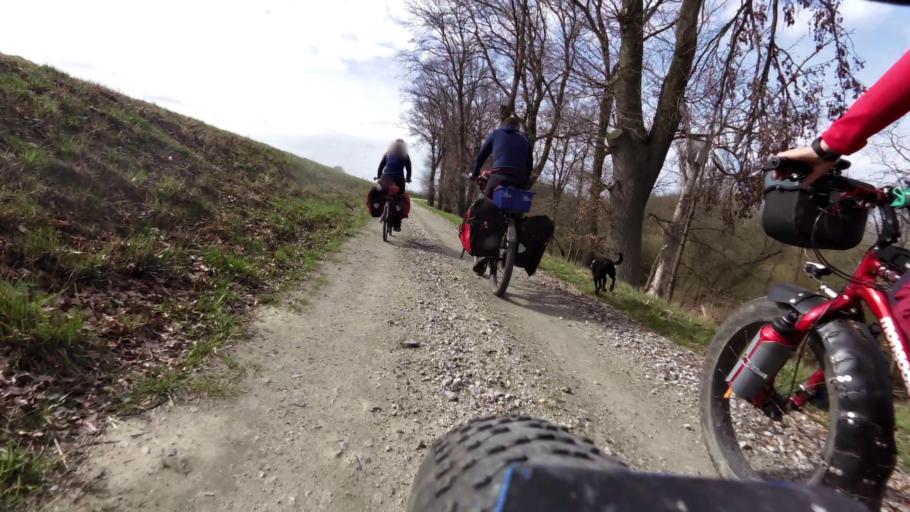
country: PL
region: Lubusz
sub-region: Powiat slubicki
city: Gorzyca
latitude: 52.5079
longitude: 14.6207
